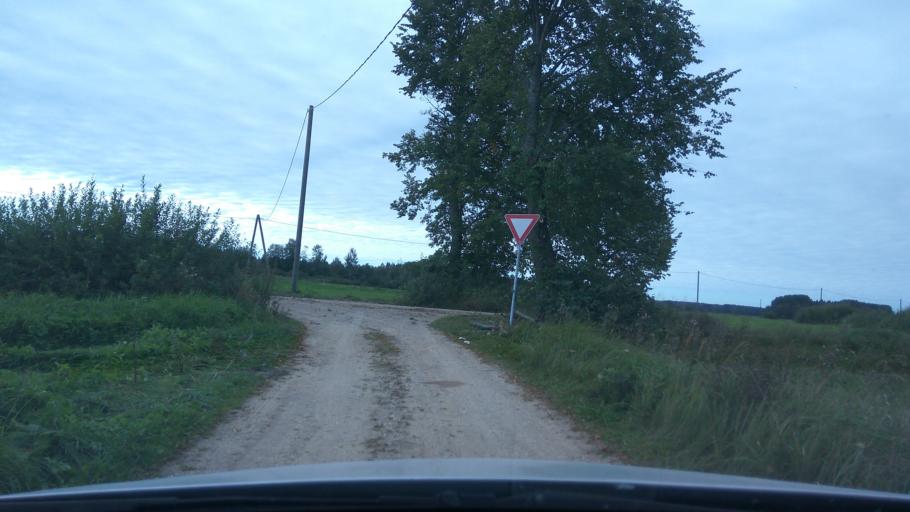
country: LV
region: Kuldigas Rajons
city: Kuldiga
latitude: 57.2420
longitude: 21.9497
